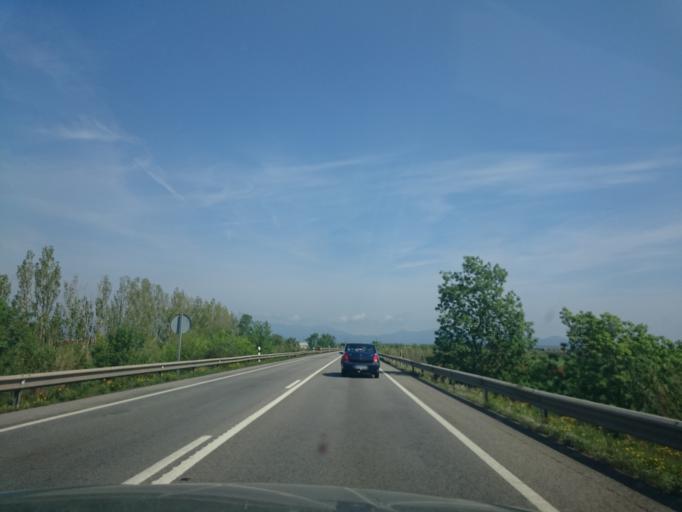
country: ES
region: Catalonia
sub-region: Provincia de Girona
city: Vilabertran
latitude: 42.2604
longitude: 2.9866
